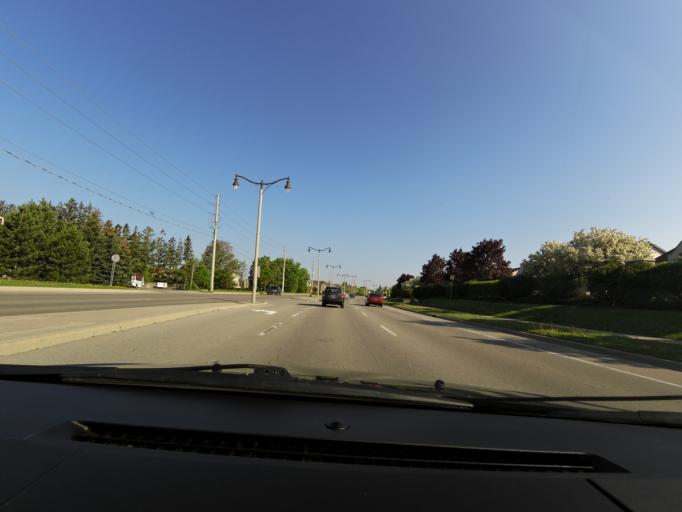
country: CA
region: Ontario
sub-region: Wellington County
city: Guelph
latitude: 43.5032
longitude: -80.1927
